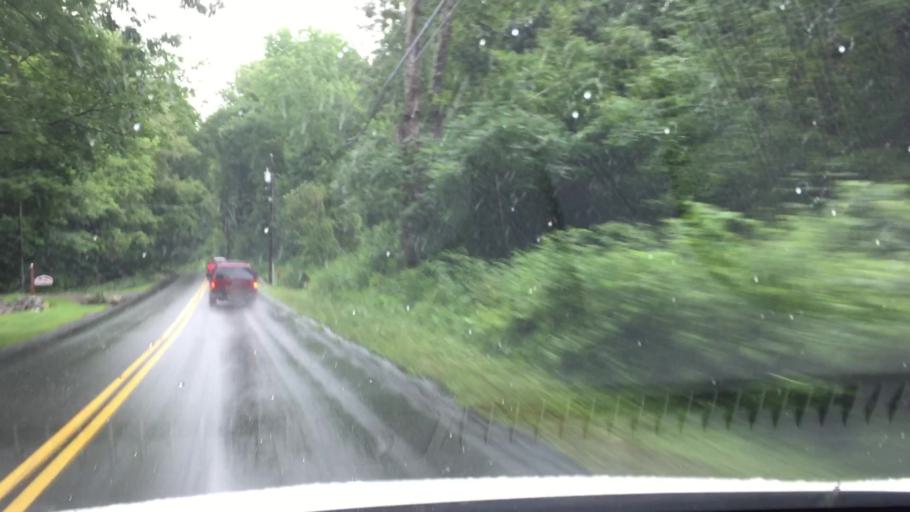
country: US
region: Massachusetts
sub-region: Berkshire County
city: Lanesborough
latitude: 42.5424
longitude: -73.2363
